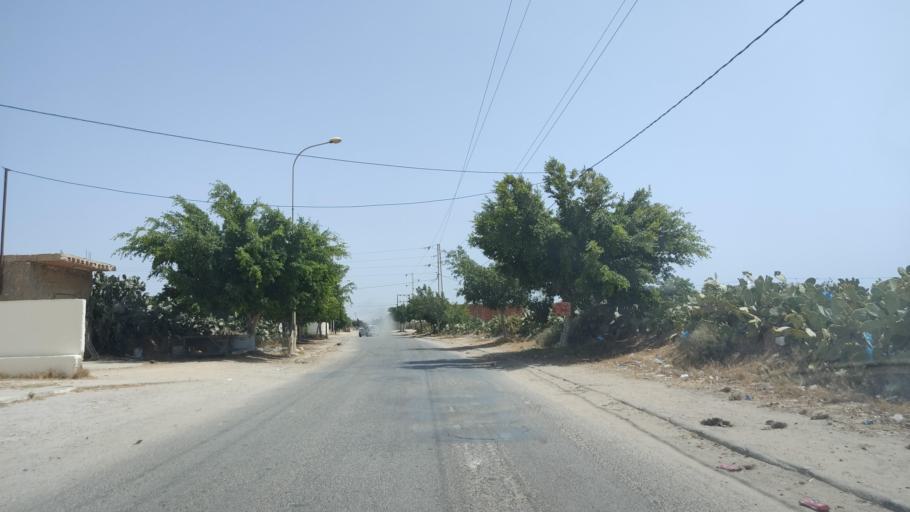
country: TN
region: Safaqis
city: Sfax
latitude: 34.6717
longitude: 10.7147
